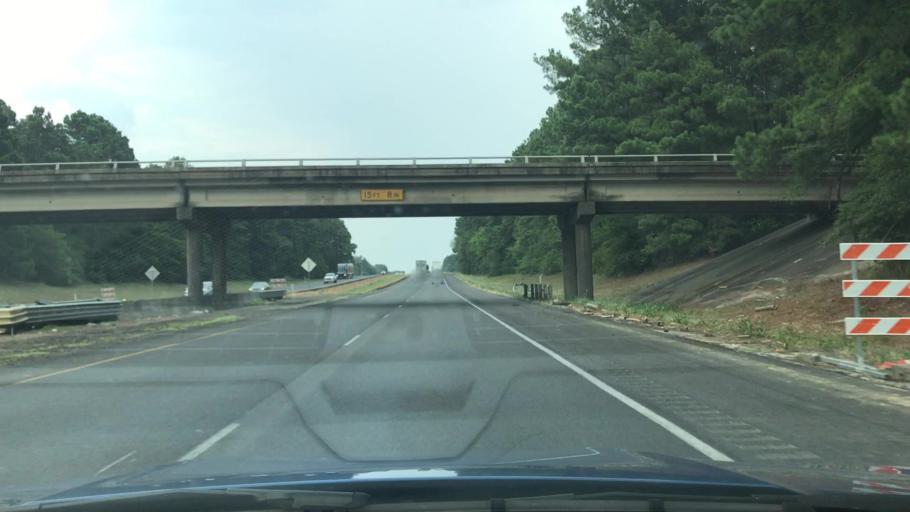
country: US
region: Texas
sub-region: Harrison County
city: Marshall
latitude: 32.4945
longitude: -94.2730
